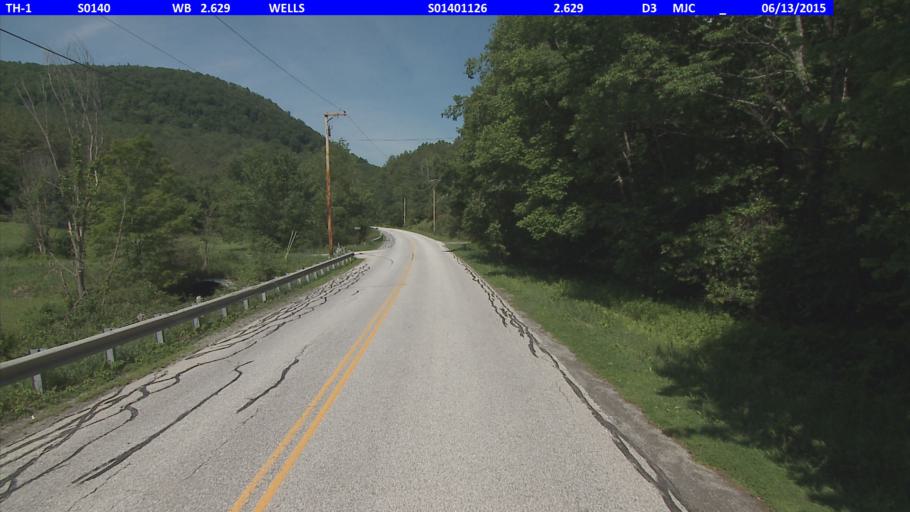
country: US
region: New York
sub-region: Washington County
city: Granville
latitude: 43.4097
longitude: -73.1558
